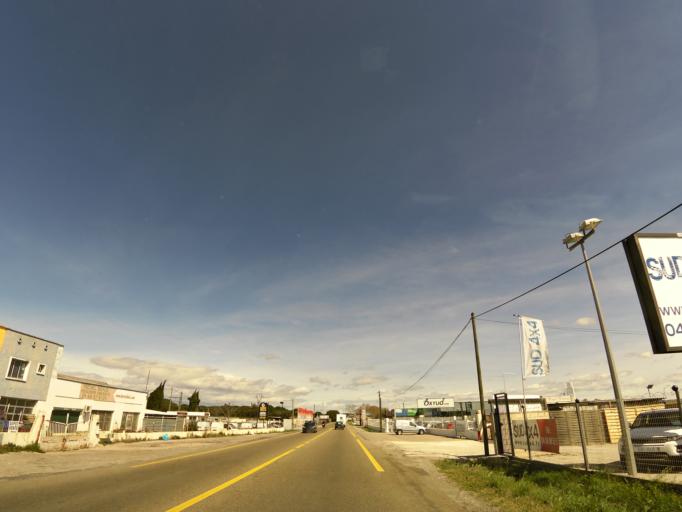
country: FR
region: Languedoc-Roussillon
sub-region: Departement du Gard
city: Bernis
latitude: 43.7760
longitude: 4.2870
